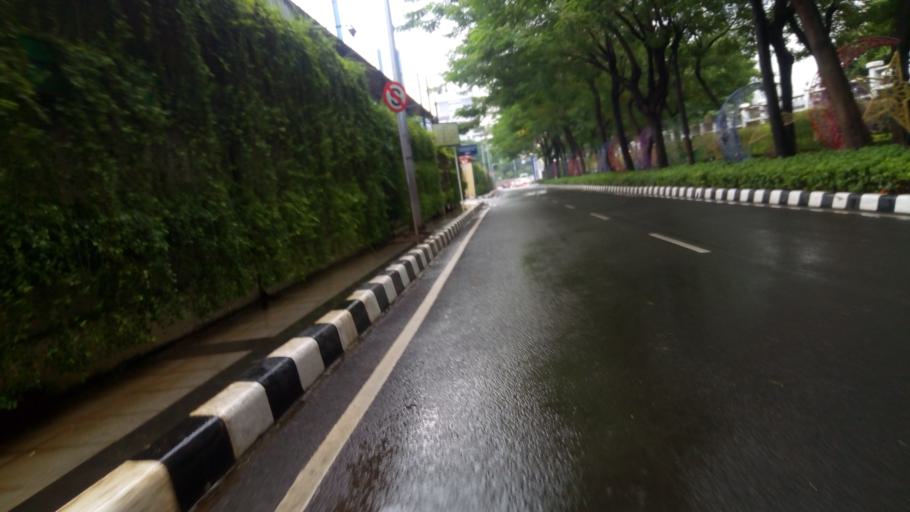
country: ID
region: Jakarta Raya
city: Jakarta
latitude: -6.2244
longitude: 106.8135
